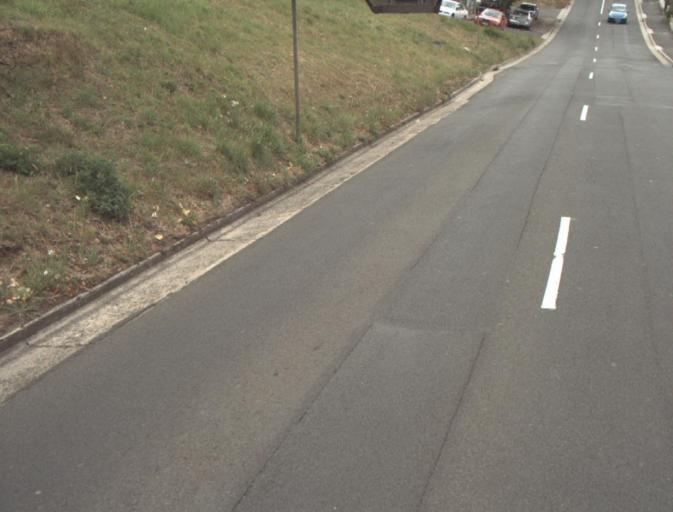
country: AU
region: Tasmania
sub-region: Launceston
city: East Launceston
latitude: -41.4467
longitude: 147.1462
